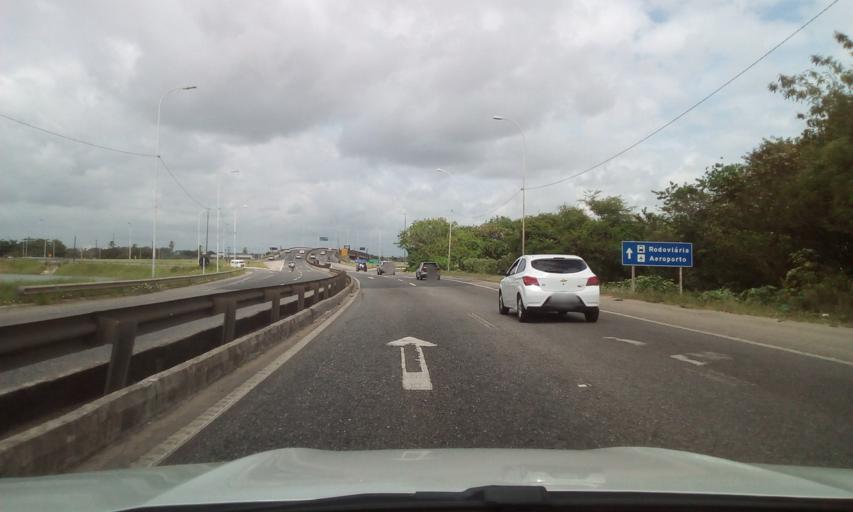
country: BR
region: Paraiba
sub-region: Bayeux
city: Bayeux
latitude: -7.1649
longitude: -34.8929
